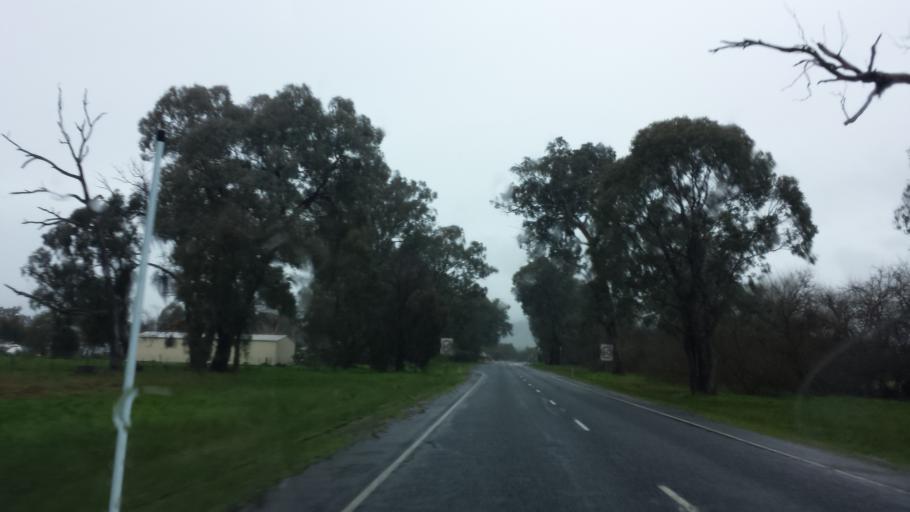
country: AU
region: Victoria
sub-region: Wangaratta
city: Wangaratta
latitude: -36.4325
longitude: 146.5371
